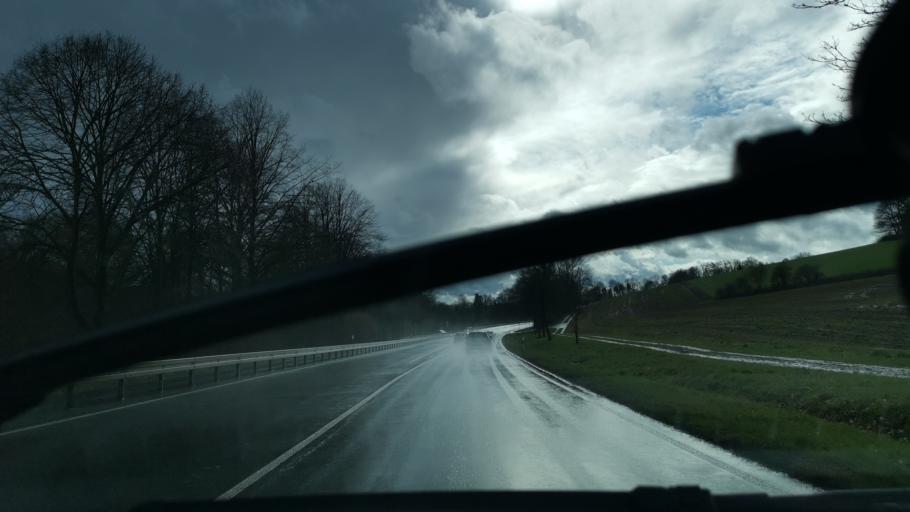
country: DE
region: Hesse
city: Bebra
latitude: 50.9863
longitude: 9.8046
